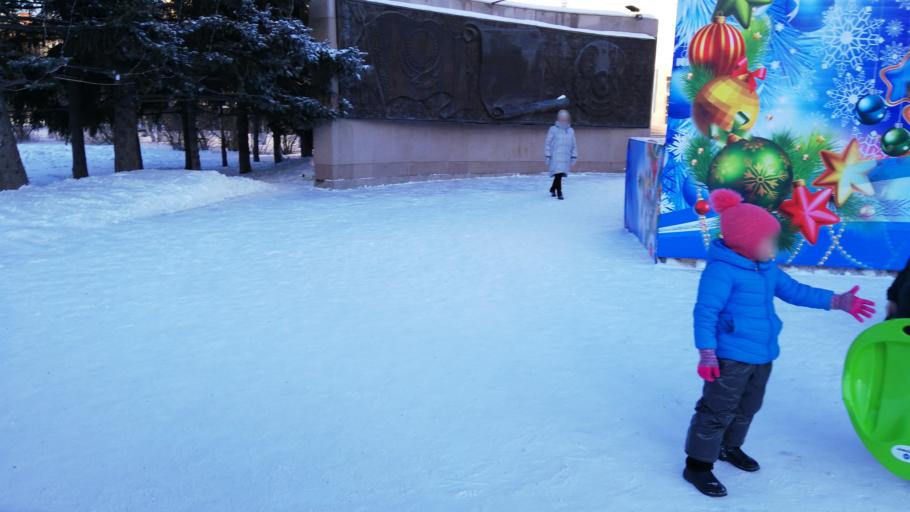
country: KZ
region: Soltustik Qazaqstan
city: Petropavlovsk
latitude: 54.8669
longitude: 69.1336
